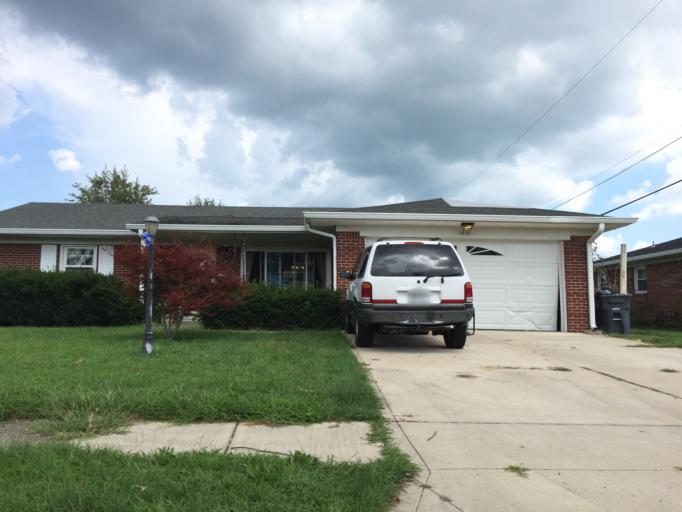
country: US
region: Indiana
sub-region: Howard County
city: Kokomo
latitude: 40.4691
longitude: -86.1020
